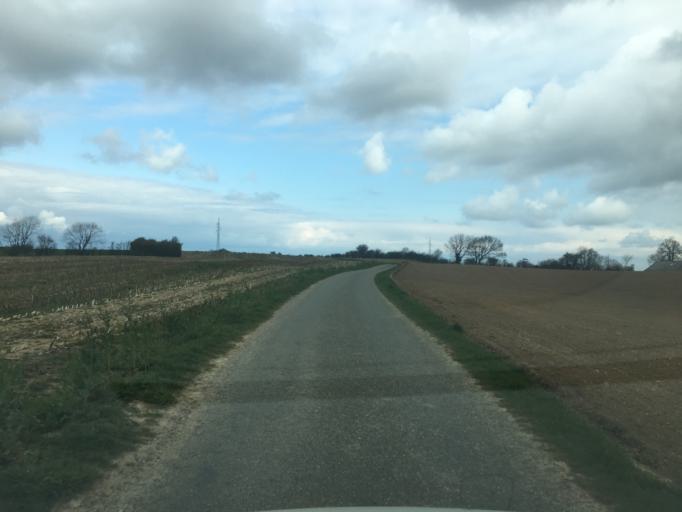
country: DK
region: South Denmark
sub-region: Sonderborg Kommune
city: Grasten
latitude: 54.9920
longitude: 9.5256
